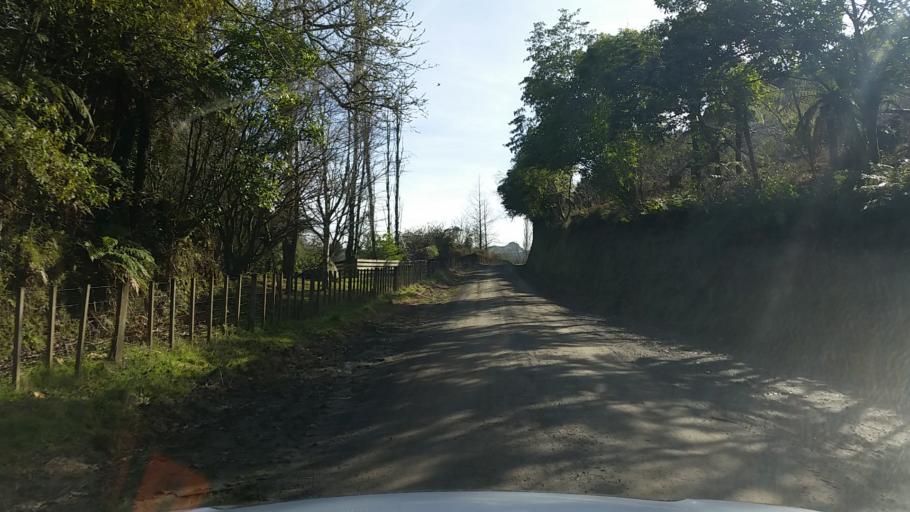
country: NZ
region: Taranaki
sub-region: South Taranaki District
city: Eltham
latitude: -39.3590
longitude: 174.5125
